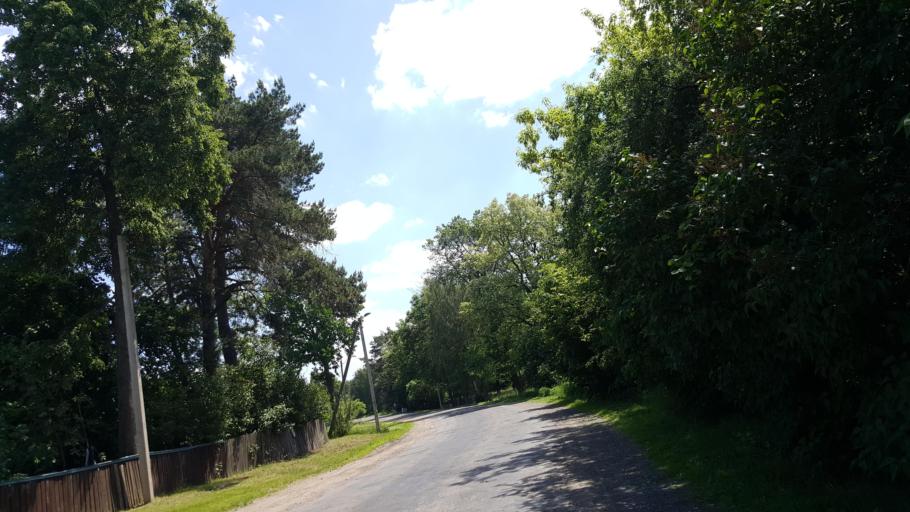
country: BY
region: Brest
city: Zhabinka
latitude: 52.1964
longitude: 24.1651
